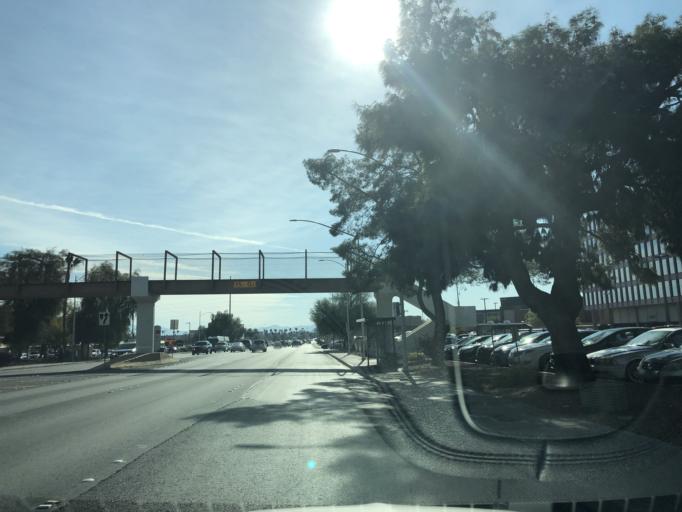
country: US
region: Nevada
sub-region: Clark County
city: Winchester
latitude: 36.1326
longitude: -115.1370
